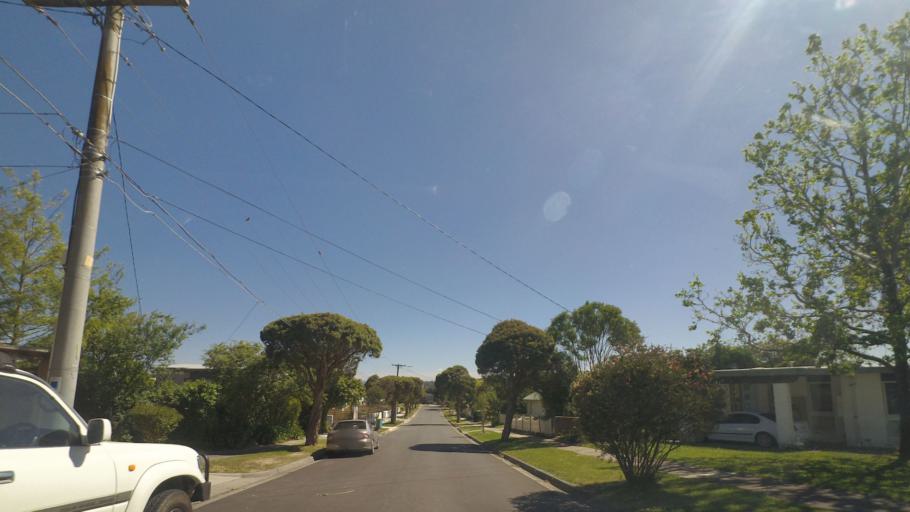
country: AU
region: Victoria
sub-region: Yarra Ranges
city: Kilsyth
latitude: -37.7977
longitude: 145.3093
